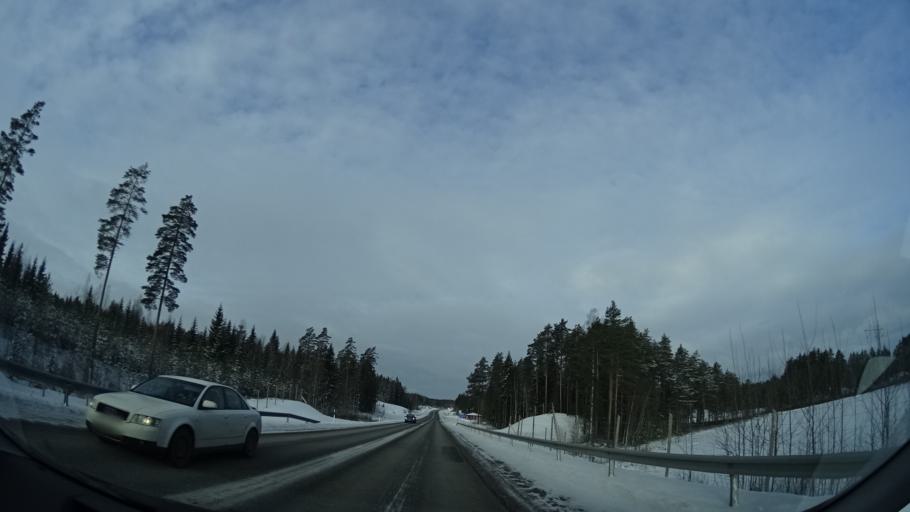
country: FI
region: Uusimaa
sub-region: Helsinki
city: Karkkila
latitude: 60.5901
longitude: 24.1117
